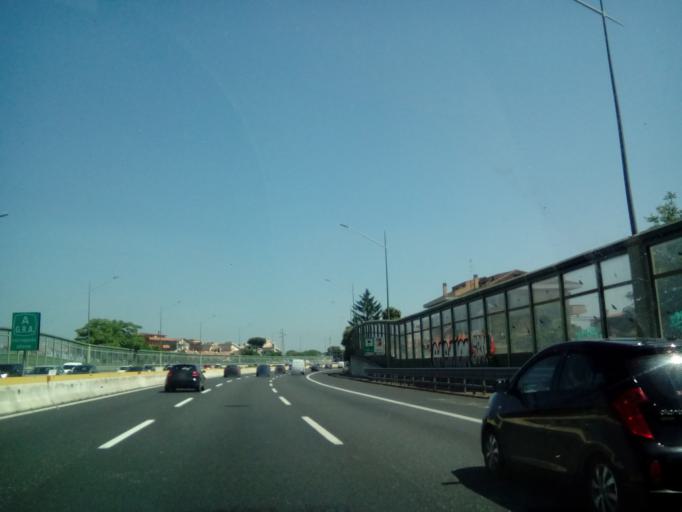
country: IT
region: Latium
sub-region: Citta metropolitana di Roma Capitale
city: Valle Santa
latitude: 41.9533
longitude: 12.3834
